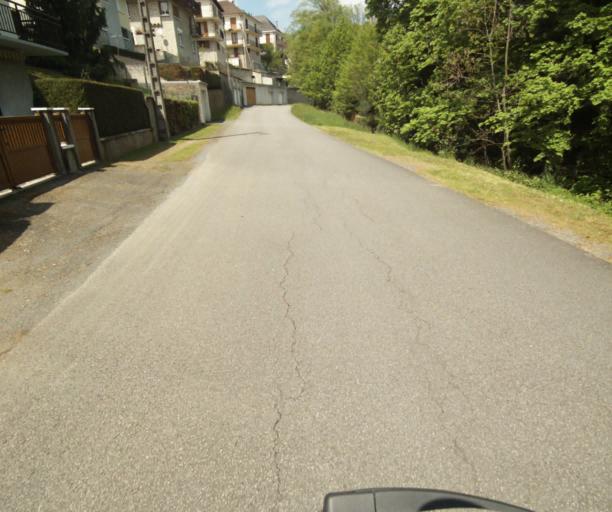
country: FR
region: Limousin
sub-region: Departement de la Correze
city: Tulle
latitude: 45.2715
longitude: 1.7656
